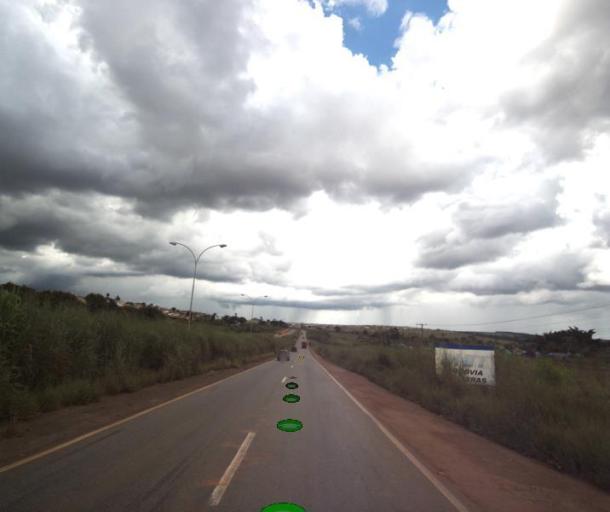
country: BR
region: Goias
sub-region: Anapolis
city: Anapolis
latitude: -16.3096
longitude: -48.9229
